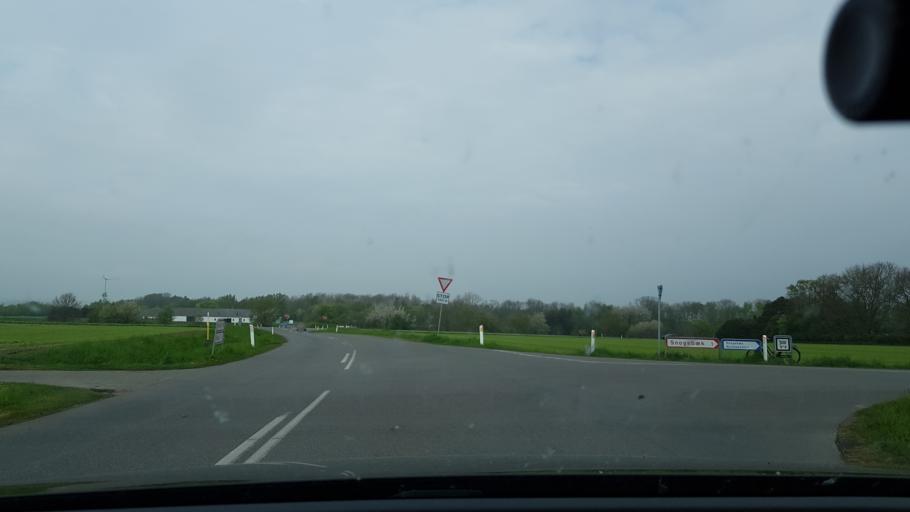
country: DK
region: Capital Region
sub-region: Bornholm Kommune
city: Nexo
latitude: 55.0225
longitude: 15.0972
